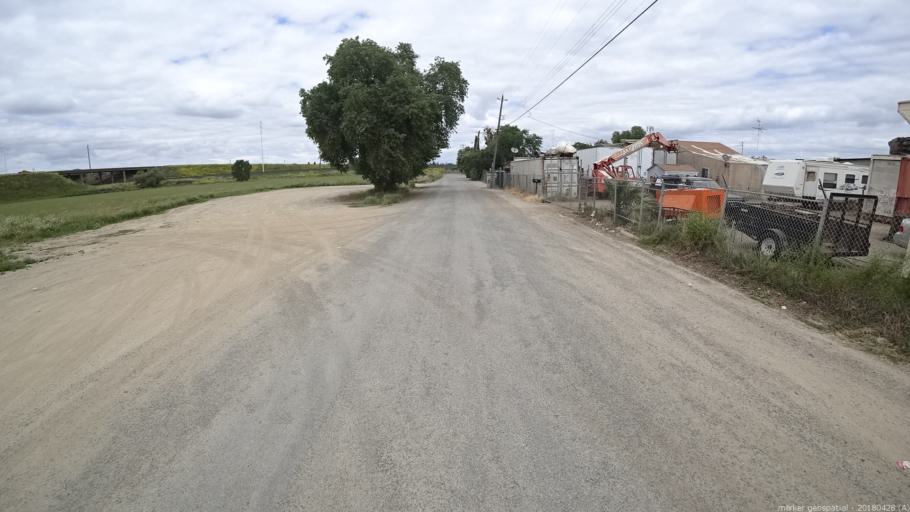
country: US
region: California
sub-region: Yolo County
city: West Sacramento
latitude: 38.5829
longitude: -121.5547
